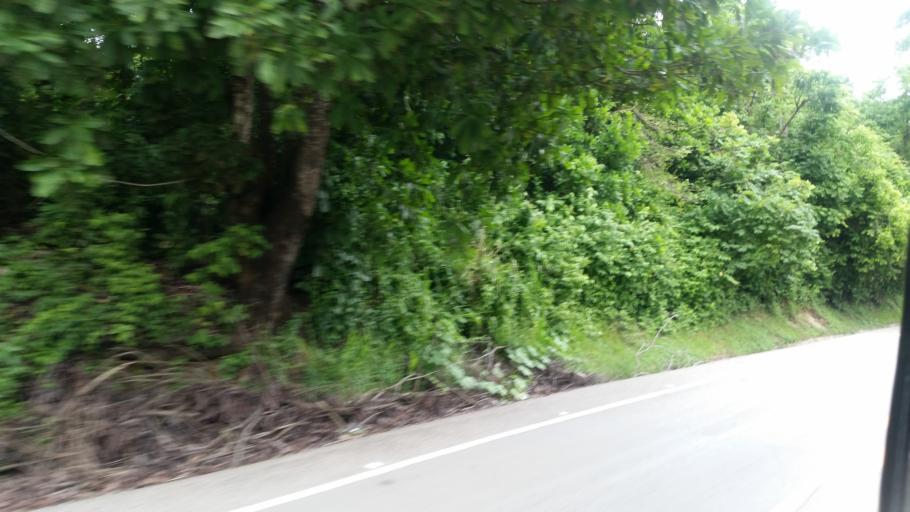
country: CO
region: Magdalena
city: Santa Marta
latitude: 11.2812
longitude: -73.9144
